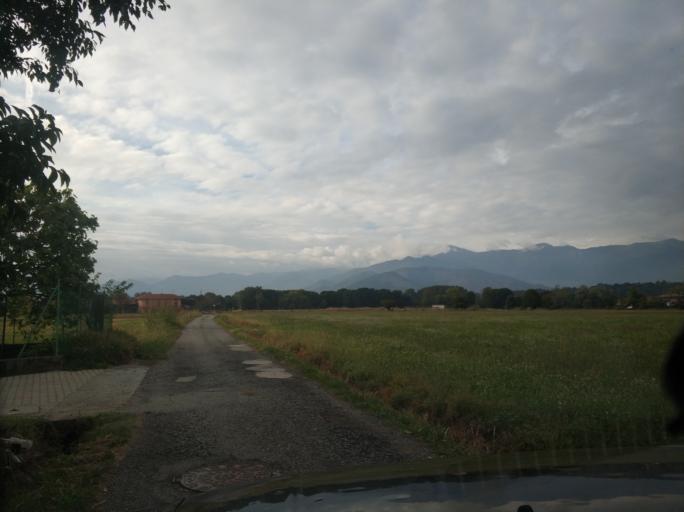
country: IT
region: Piedmont
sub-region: Provincia di Torino
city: Nole
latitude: 45.2484
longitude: 7.5711
